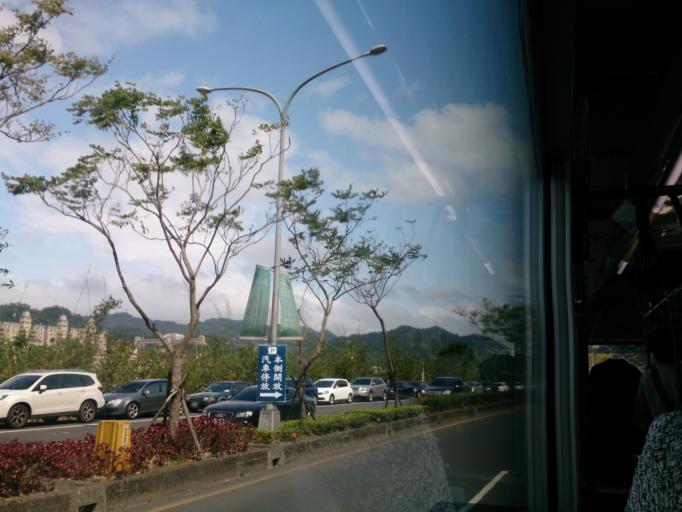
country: TW
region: Taipei
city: Taipei
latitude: 25.0085
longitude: 121.6343
